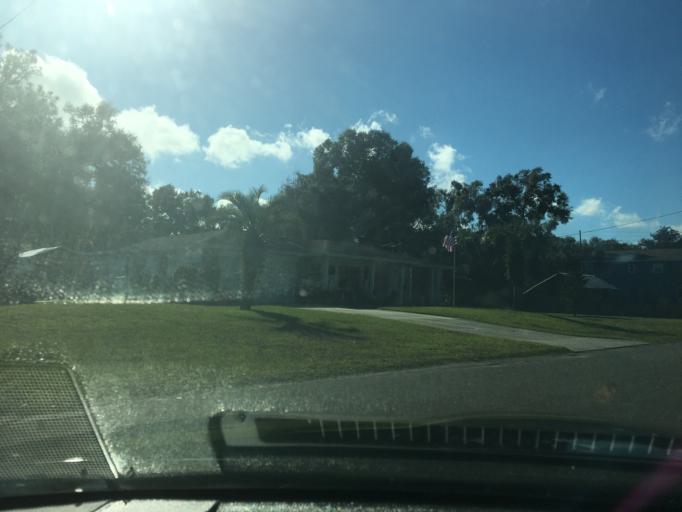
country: US
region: Florida
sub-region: Citrus County
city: Inverness
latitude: 28.8303
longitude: -82.3290
